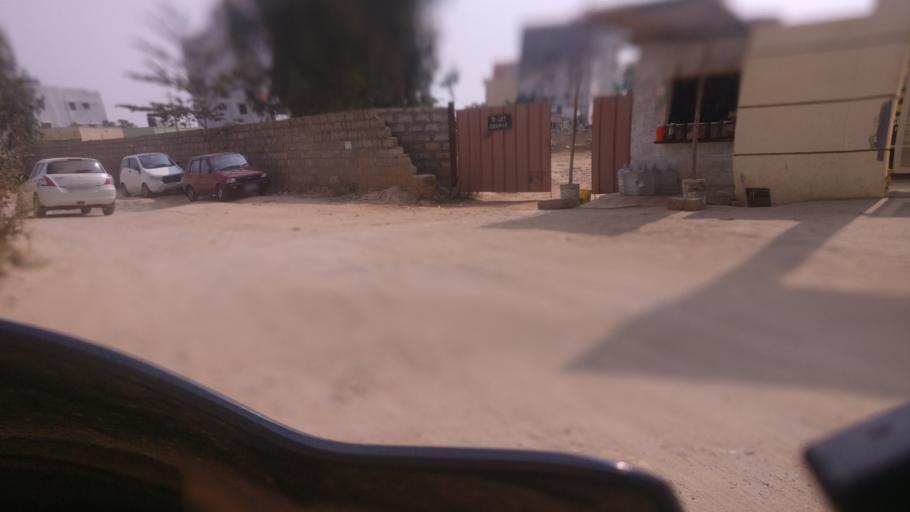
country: IN
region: Karnataka
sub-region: Bangalore Urban
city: Bangalore
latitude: 12.8961
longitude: 77.6787
